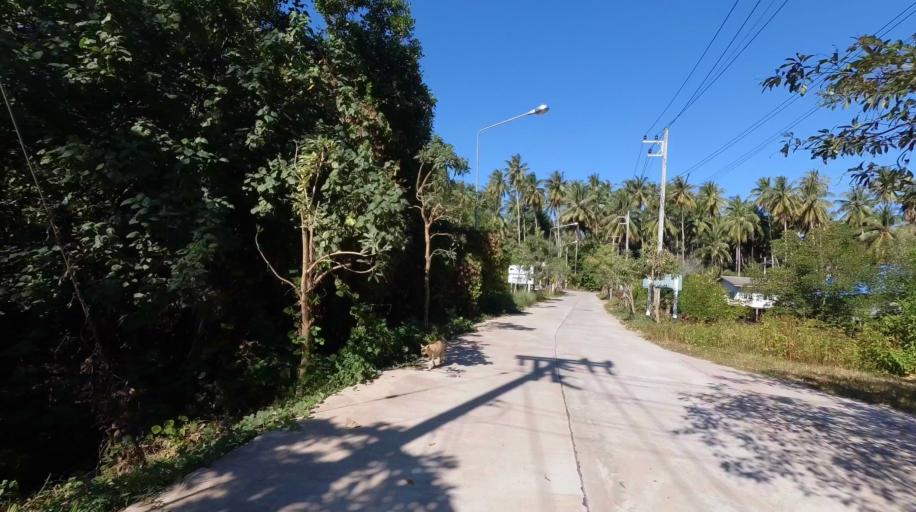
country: TH
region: Trat
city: Ko Kut
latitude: 11.6218
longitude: 102.5475
